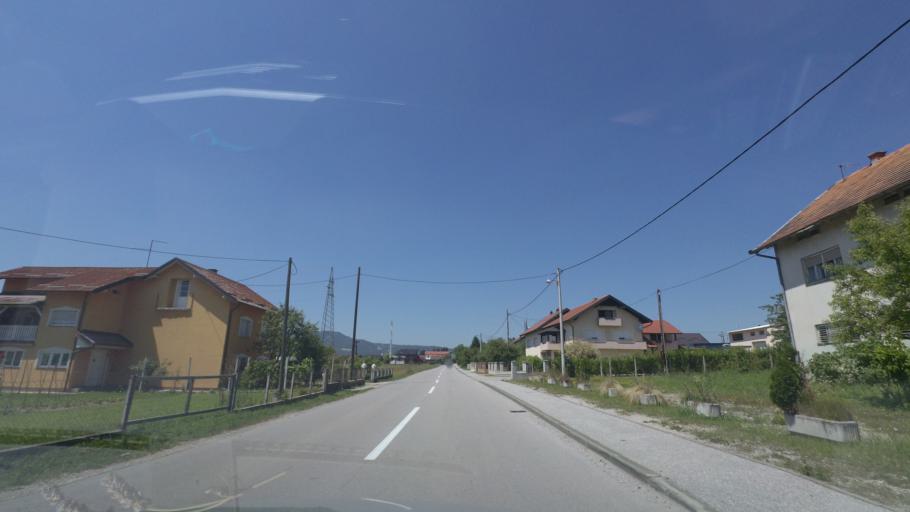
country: HR
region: Grad Zagreb
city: Horvati
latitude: 45.6880
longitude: 15.7460
